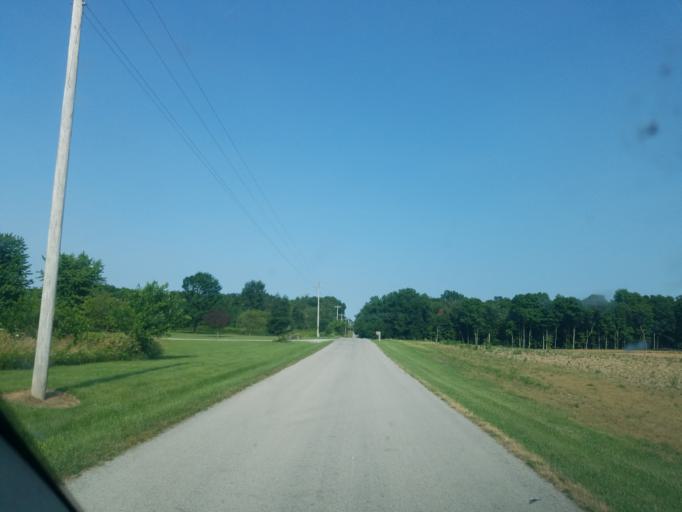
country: US
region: Ohio
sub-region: Crawford County
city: Bucyrus
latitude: 40.8919
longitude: -83.1237
